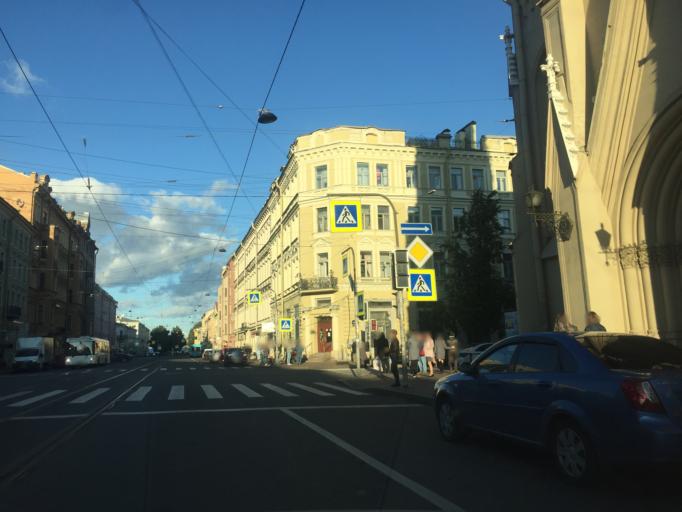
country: RU
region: St.-Petersburg
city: Vasyl'evsky Ostrov
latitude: 59.9445
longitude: 30.2832
